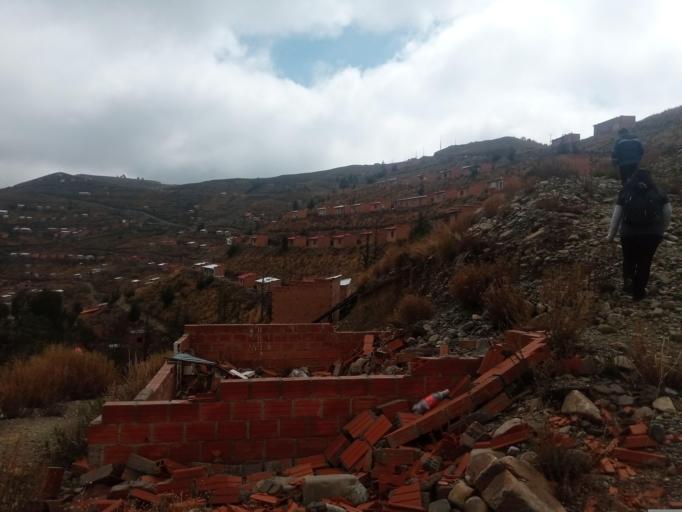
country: BO
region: La Paz
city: La Paz
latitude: -16.4658
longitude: -68.1496
